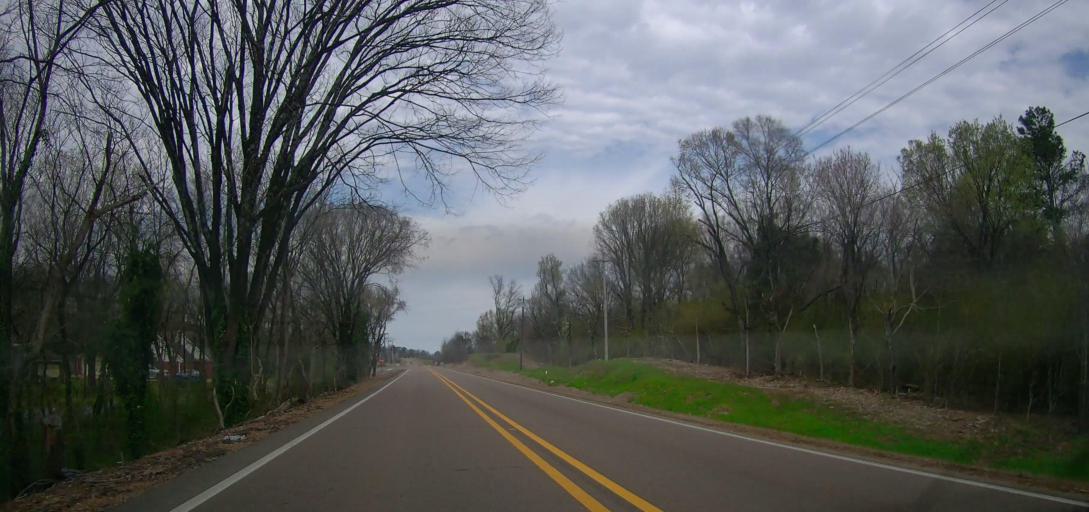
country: US
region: Mississippi
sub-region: De Soto County
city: Olive Branch
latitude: 34.9721
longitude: -89.8401
